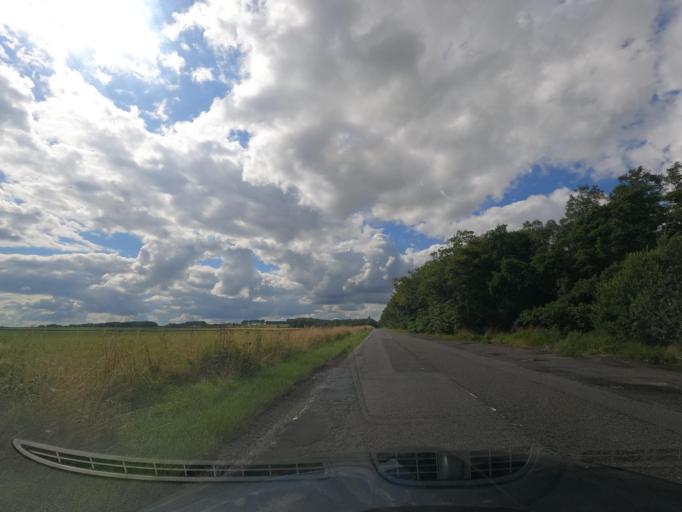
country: GB
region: Scotland
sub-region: The Scottish Borders
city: Earlston
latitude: 55.7187
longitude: -2.6087
